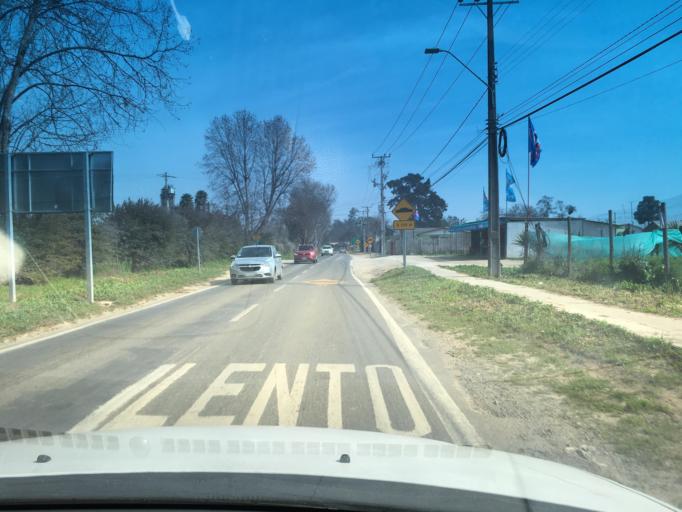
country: CL
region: Valparaiso
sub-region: Provincia de Marga Marga
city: Limache
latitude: -33.0121
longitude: -71.2002
